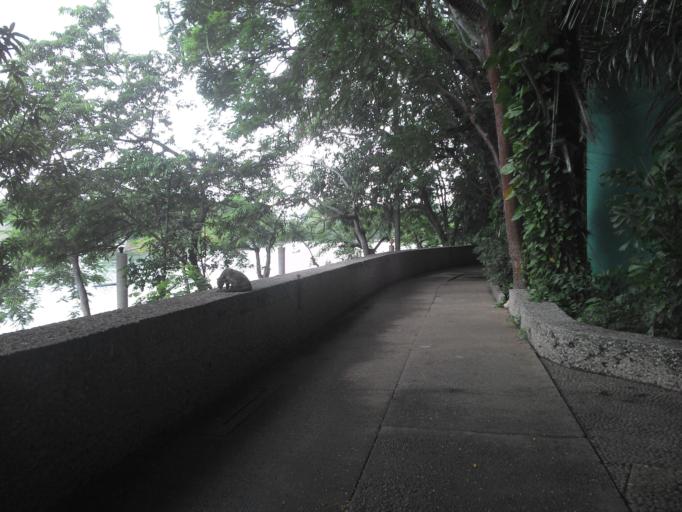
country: MX
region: Tabasco
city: Villahermosa
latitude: 18.0009
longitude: -92.9336
